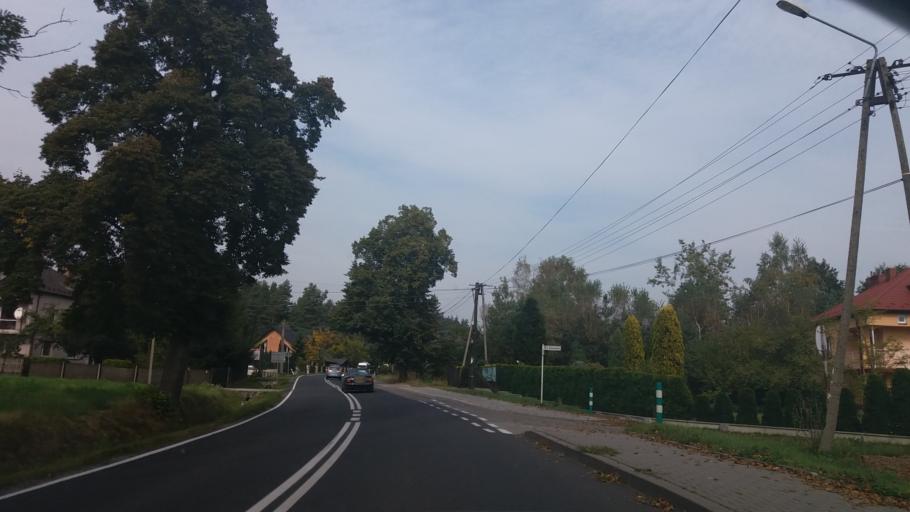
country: PL
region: Lesser Poland Voivodeship
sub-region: Powiat chrzanowski
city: Babice
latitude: 50.0551
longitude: 19.4531
